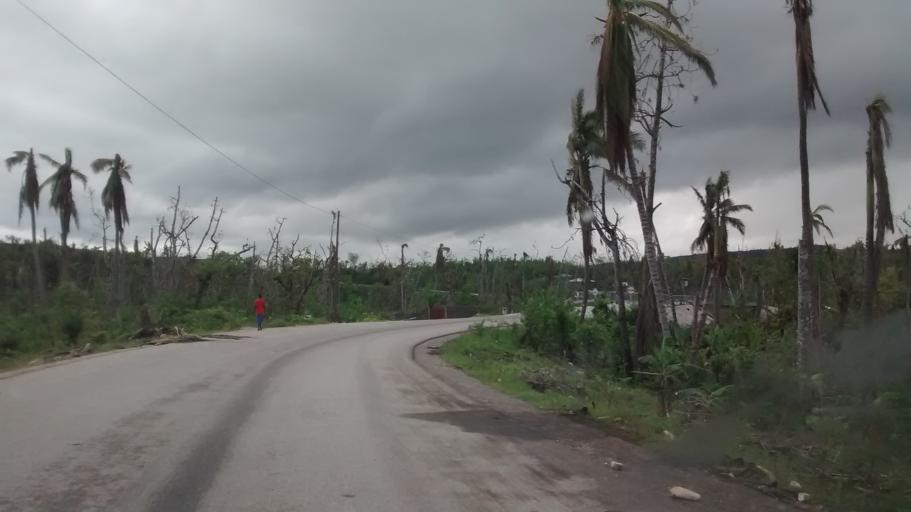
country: HT
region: Grandans
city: Jeremie
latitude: 18.6166
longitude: -74.0876
